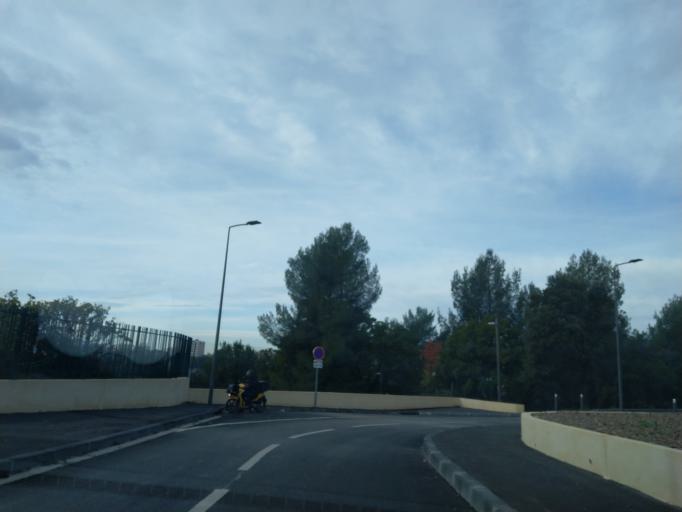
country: FR
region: Provence-Alpes-Cote d'Azur
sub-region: Departement des Bouches-du-Rhone
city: Marseille 12
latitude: 43.2981
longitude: 5.4448
